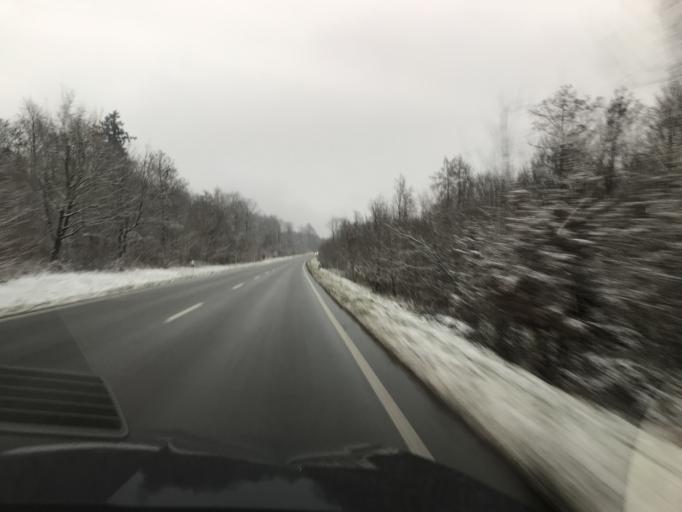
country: DE
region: Baden-Wuerttemberg
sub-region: Regierungsbezirk Stuttgart
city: Altbach
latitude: 48.7435
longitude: 9.3639
